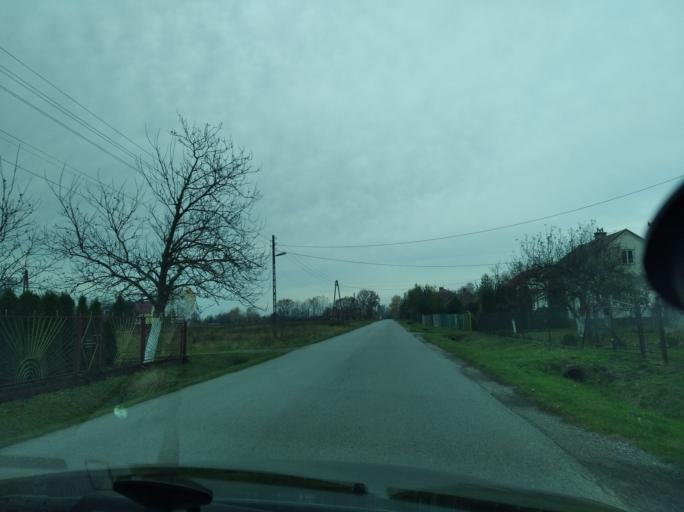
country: PL
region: Subcarpathian Voivodeship
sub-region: Powiat przeworski
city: Grzeska
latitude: 50.0923
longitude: 22.4442
